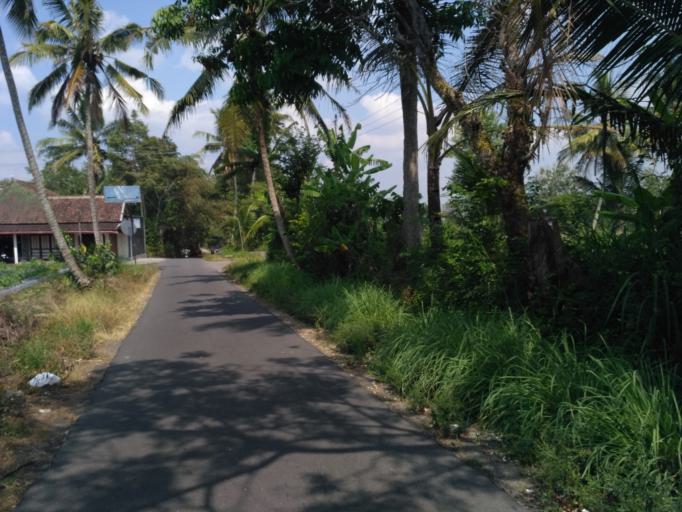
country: ID
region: Daerah Istimewa Yogyakarta
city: Depok
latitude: -7.7148
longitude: 110.4237
